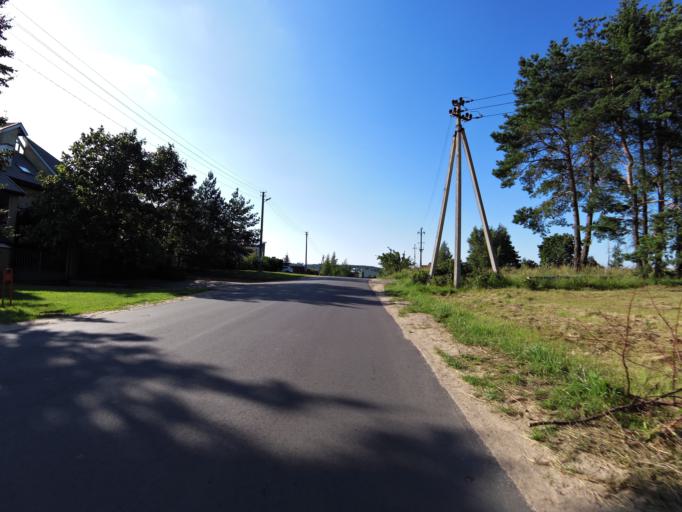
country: LT
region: Vilnius County
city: Pasilaiciai
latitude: 54.7302
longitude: 25.1903
